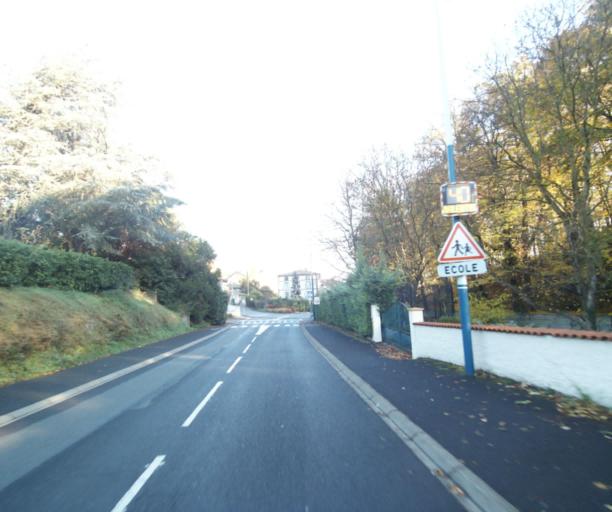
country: FR
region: Auvergne
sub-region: Departement du Puy-de-Dome
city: Nohanent
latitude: 45.8072
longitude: 3.0540
